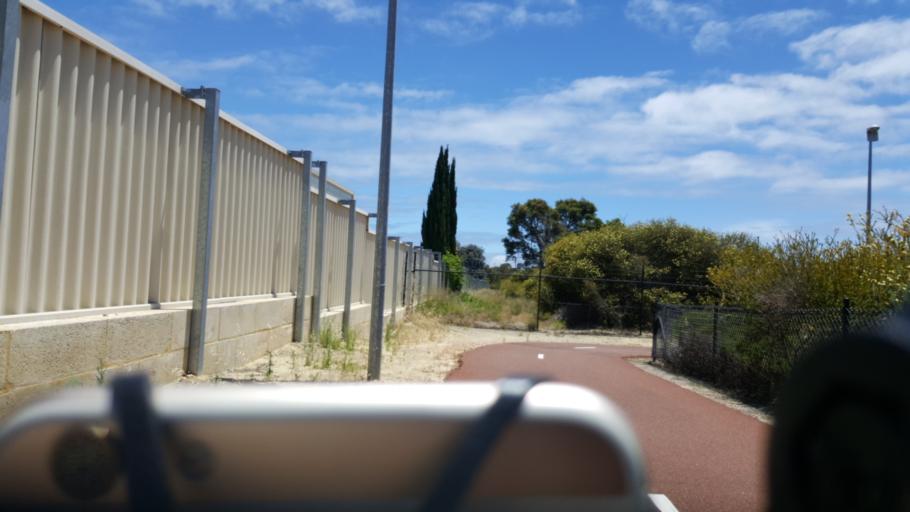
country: AU
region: Western Australia
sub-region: Stirling
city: Westminster
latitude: -31.8667
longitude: 115.8659
